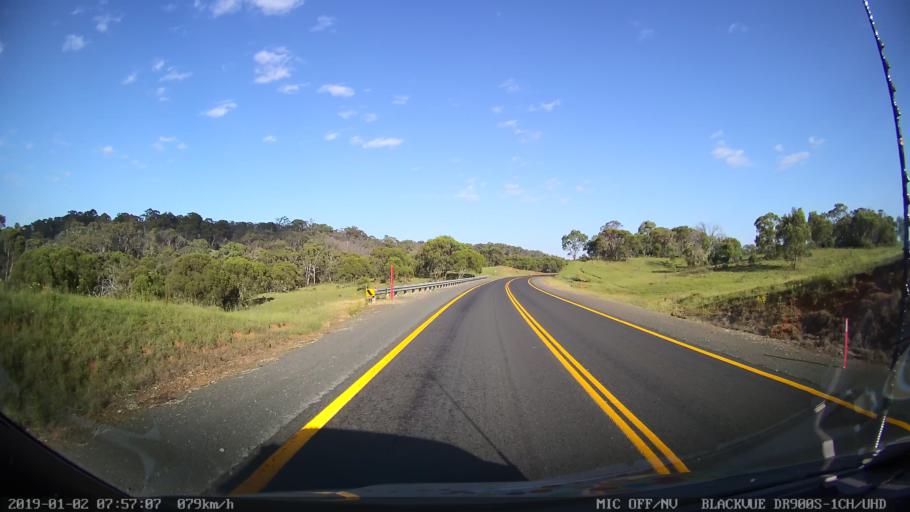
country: AU
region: New South Wales
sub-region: Tumut Shire
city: Tumut
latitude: -35.6665
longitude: 148.4769
